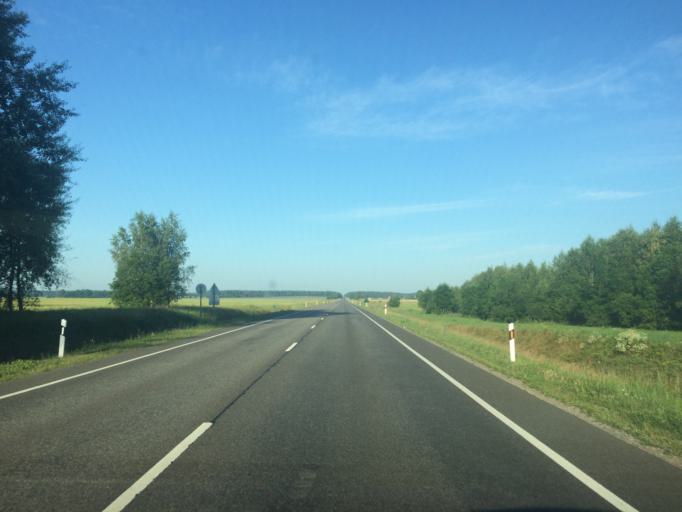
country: LT
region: Vilnius County
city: Ukmerge
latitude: 55.2050
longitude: 24.6331
